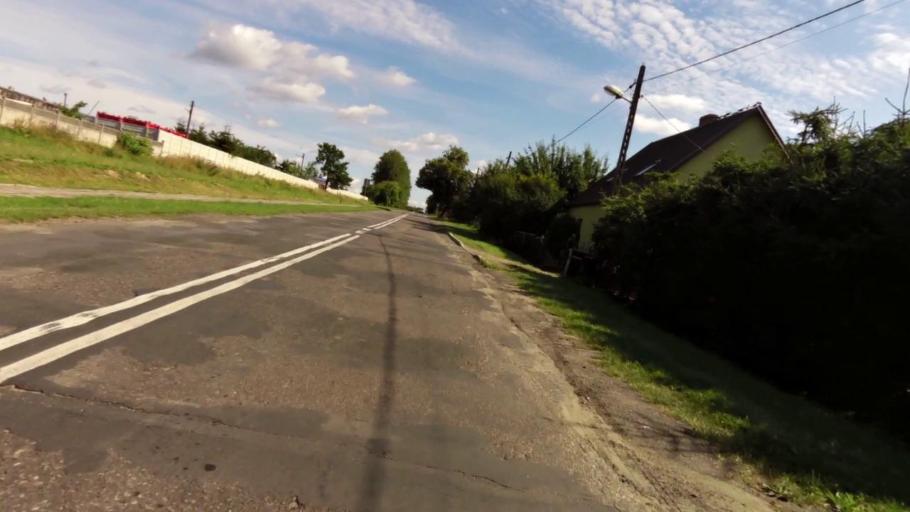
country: PL
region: West Pomeranian Voivodeship
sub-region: Powiat stargardzki
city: Dobrzany
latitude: 53.3653
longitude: 15.4285
